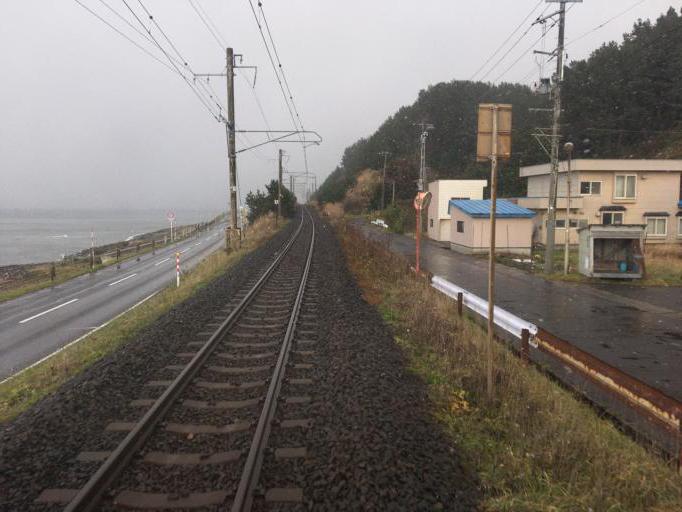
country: JP
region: Aomori
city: Aomori Shi
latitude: 41.0330
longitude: 140.6459
